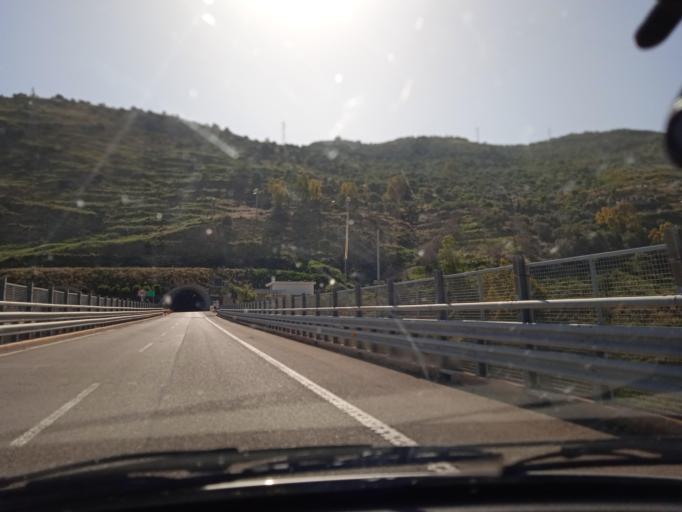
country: IT
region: Sicily
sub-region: Messina
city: Santo Stefano di Camastra
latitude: 38.0043
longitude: 14.3460
